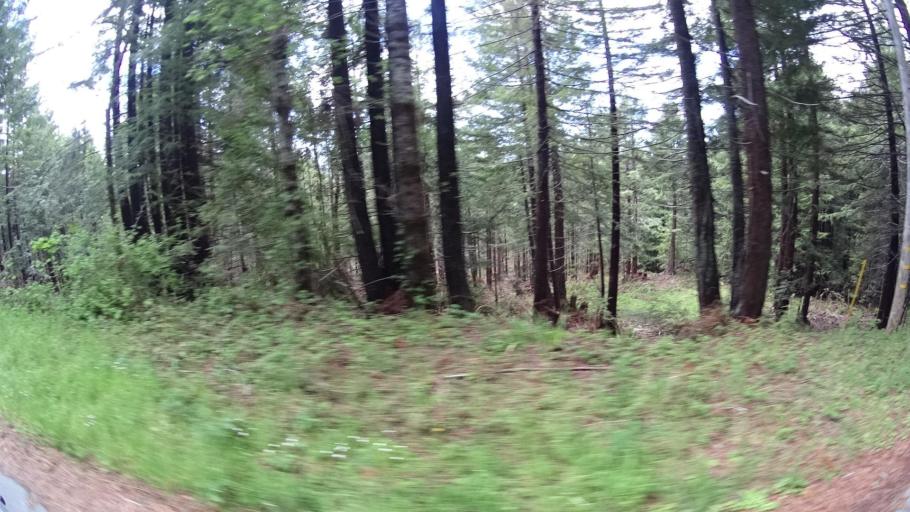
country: US
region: California
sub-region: Humboldt County
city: Blue Lake
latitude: 40.8529
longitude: -123.9294
